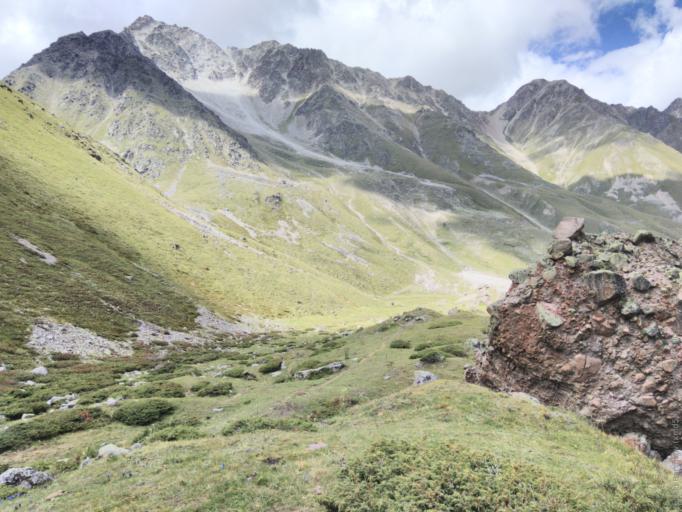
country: RU
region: Kabardino-Balkariya
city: Terskol
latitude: 43.3577
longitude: 42.3307
